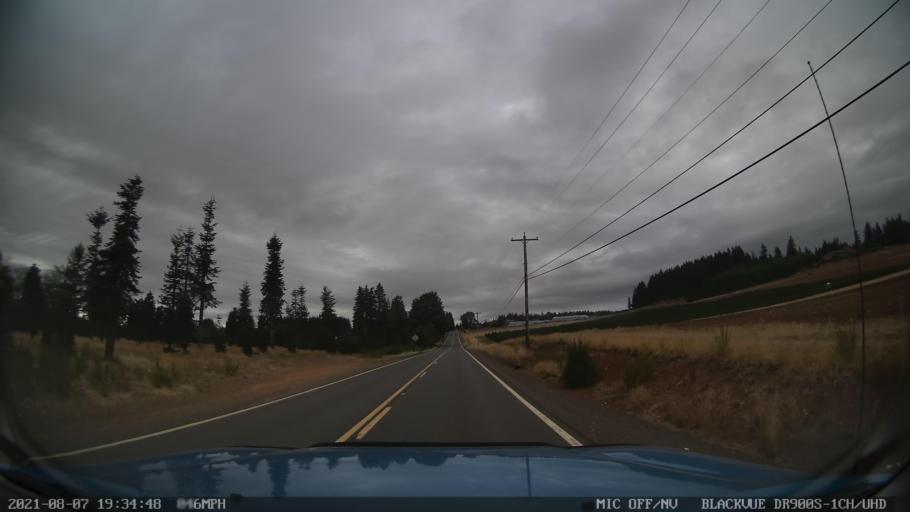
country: US
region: Oregon
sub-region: Marion County
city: Silverton
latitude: 44.9215
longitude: -122.6567
